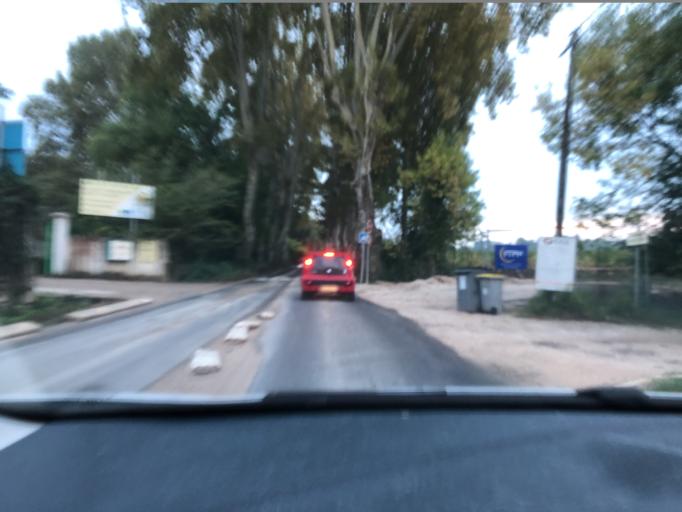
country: FR
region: Languedoc-Roussillon
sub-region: Departement de l'Herault
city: Montferrier-sur-Lez
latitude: 43.6625
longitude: 3.8629
